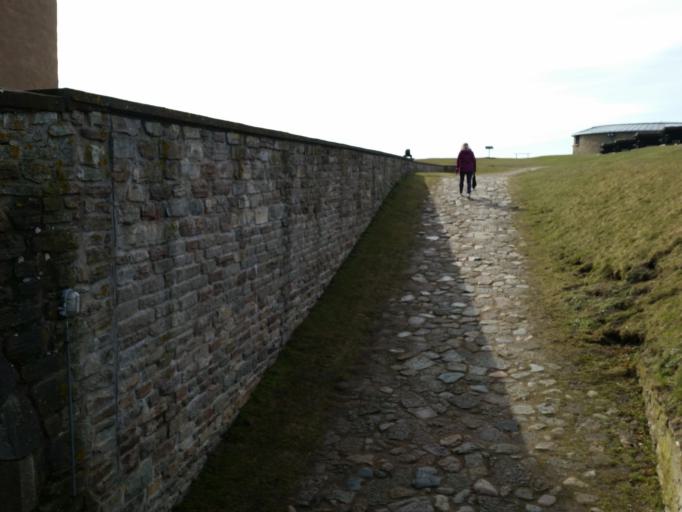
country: SE
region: Kalmar
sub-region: Kalmar Kommun
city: Kalmar
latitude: 56.6581
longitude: 16.3547
